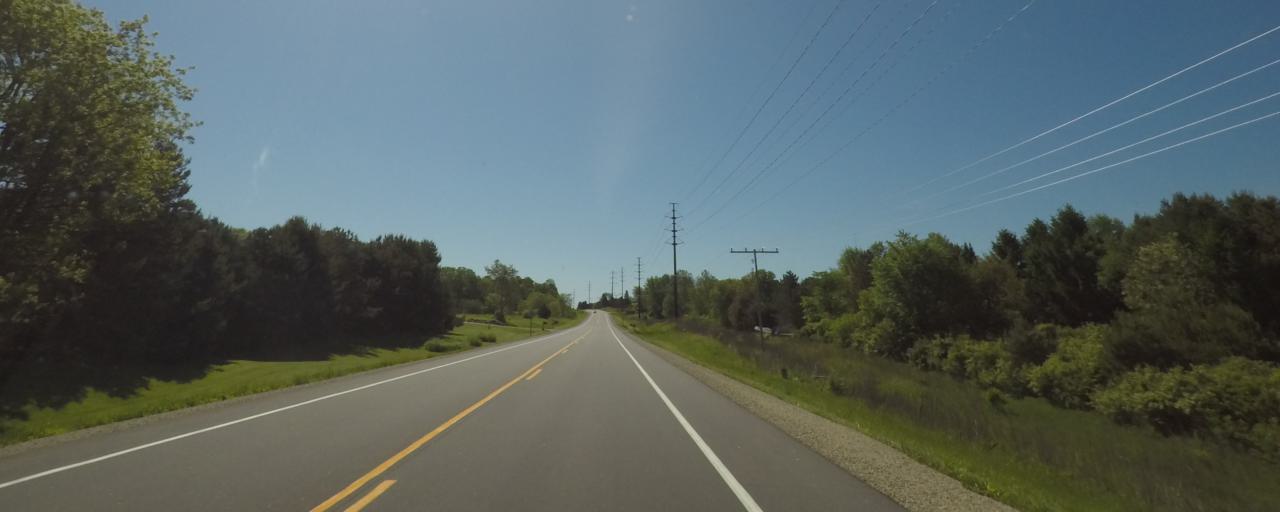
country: US
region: Wisconsin
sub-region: Dane County
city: Fitchburg
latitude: 42.9706
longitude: -89.4992
